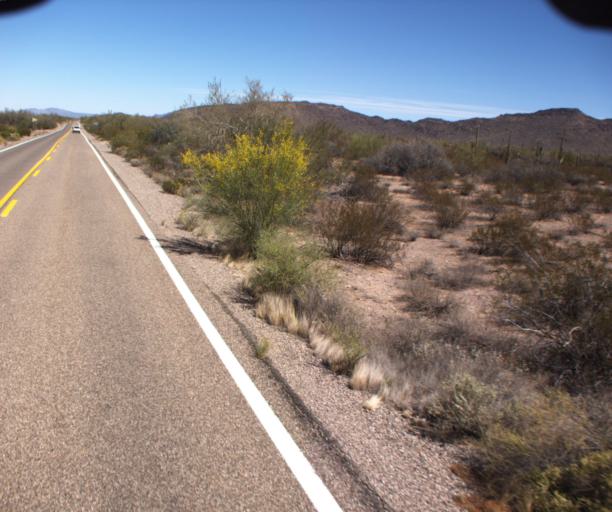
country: US
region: Arizona
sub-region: Pima County
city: Ajo
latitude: 32.1807
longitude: -112.7617
